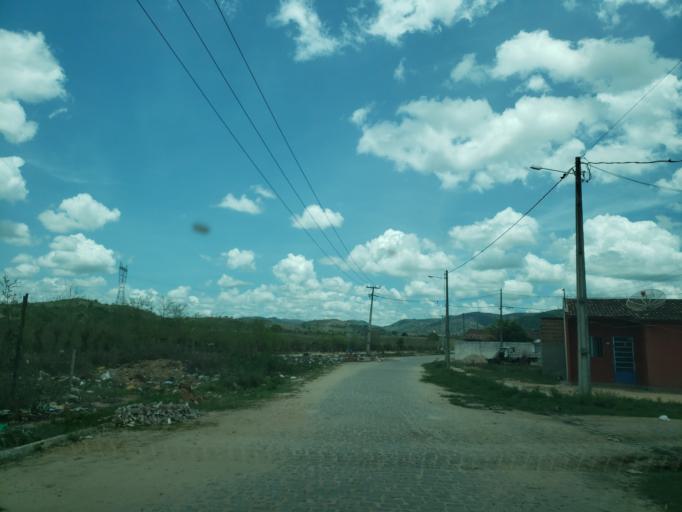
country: BR
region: Alagoas
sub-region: Uniao Dos Palmares
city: Uniao dos Palmares
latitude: -9.1492
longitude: -36.0114
